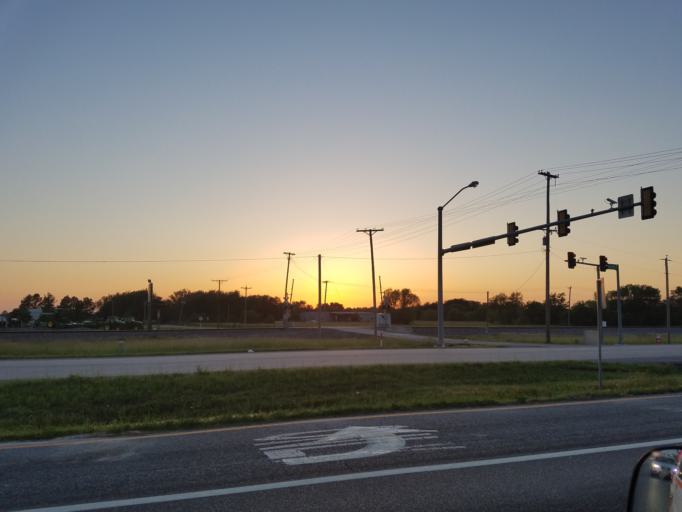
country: US
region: Oklahoma
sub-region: Mayes County
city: Pryor
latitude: 36.2511
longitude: -95.3349
